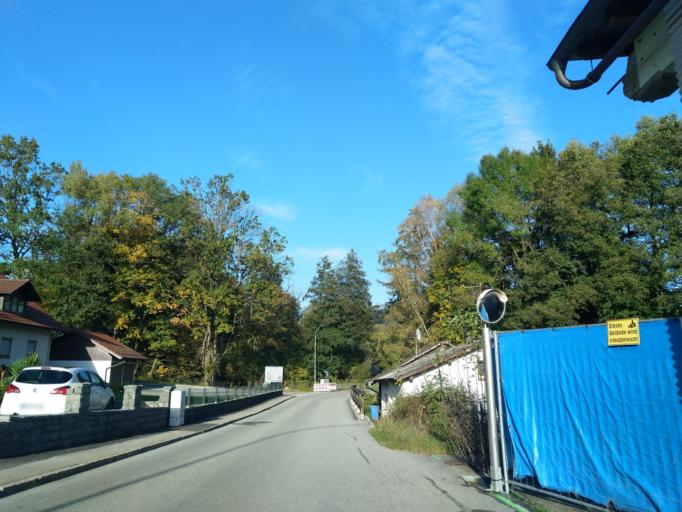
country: DE
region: Bavaria
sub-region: Lower Bavaria
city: Metten
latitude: 48.8793
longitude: 12.9197
